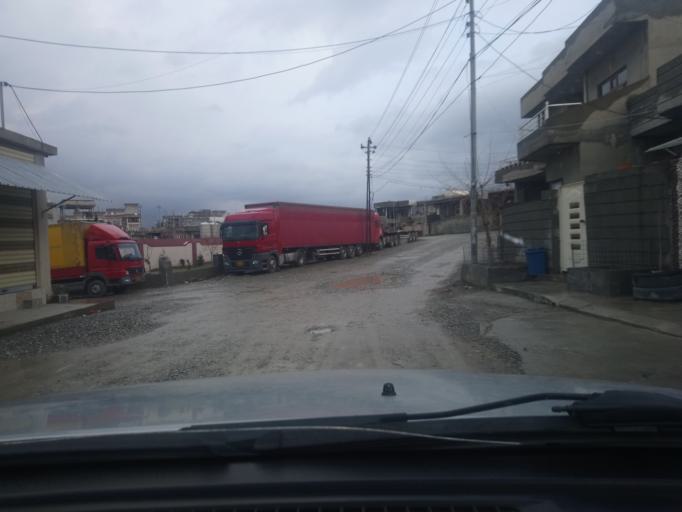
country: IQ
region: As Sulaymaniyah
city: Qeladize
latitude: 36.1913
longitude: 45.1236
